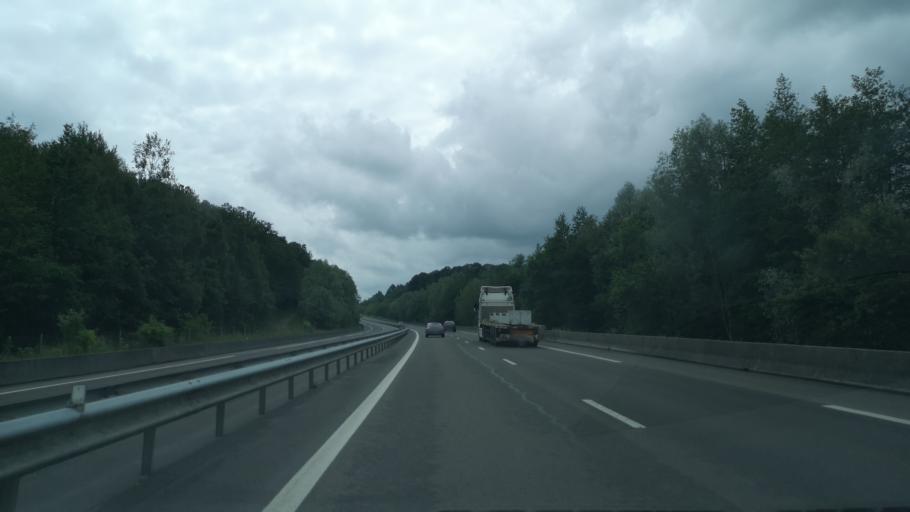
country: FR
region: Champagne-Ardenne
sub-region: Departement des Ardennes
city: Attigny
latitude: 49.6368
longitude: 4.5639
